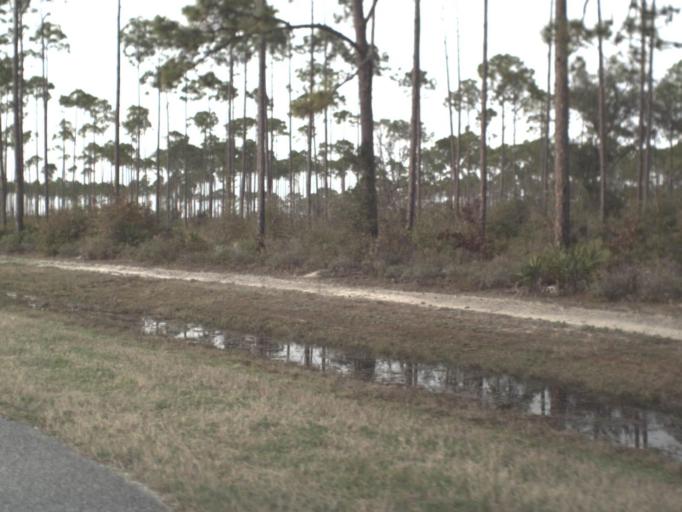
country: US
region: Florida
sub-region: Bay County
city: Tyndall Air Force Base
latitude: 30.0446
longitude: -85.5572
